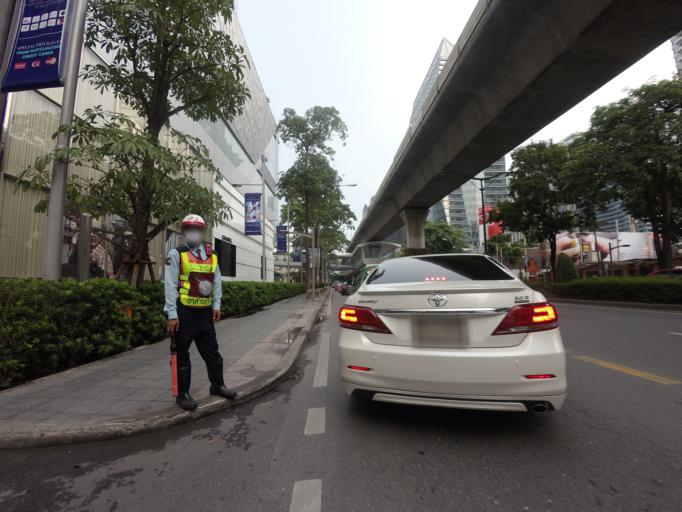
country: TH
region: Bangkok
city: Ratchathewi
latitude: 13.7430
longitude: 100.5457
